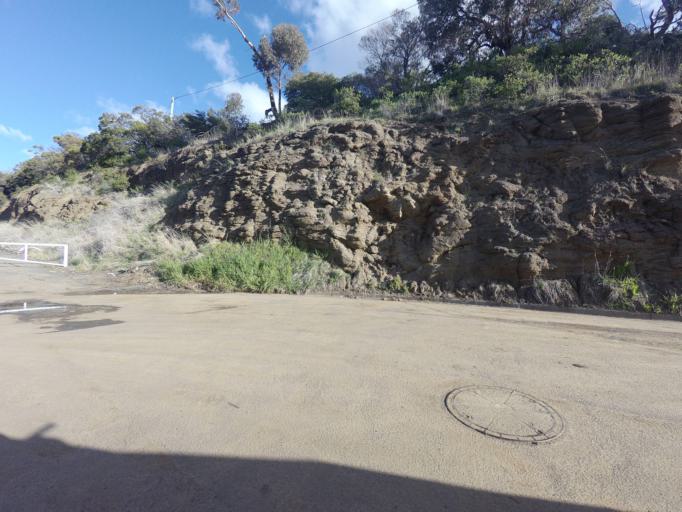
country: AU
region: Tasmania
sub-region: Hobart
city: New Town
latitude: -42.8487
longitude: 147.3260
